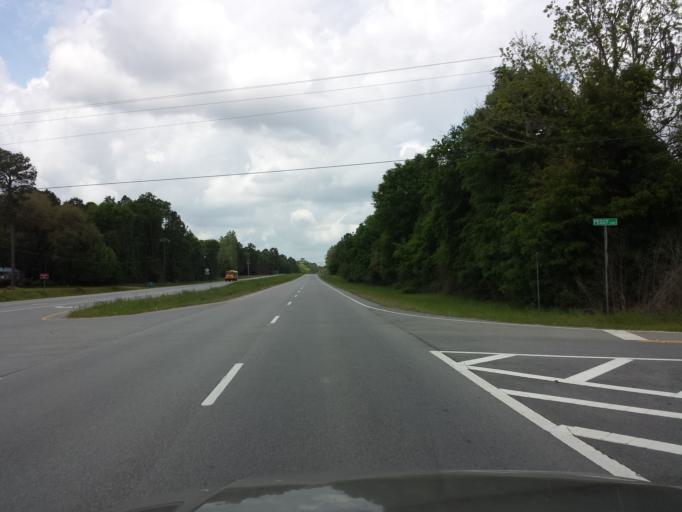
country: US
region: Georgia
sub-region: Lowndes County
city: Valdosta
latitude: 30.7103
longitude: -83.2133
